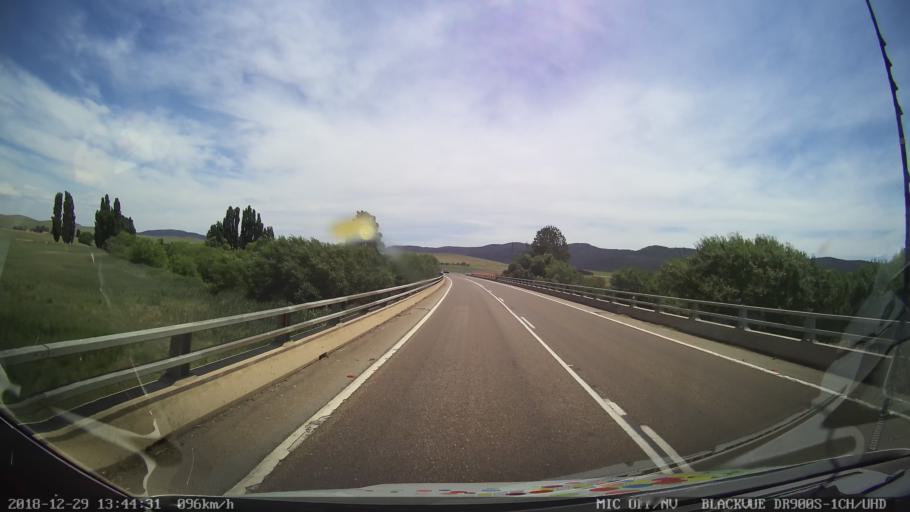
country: AU
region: New South Wales
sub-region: Cooma-Monaro
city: Cooma
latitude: -36.0842
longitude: 149.1510
